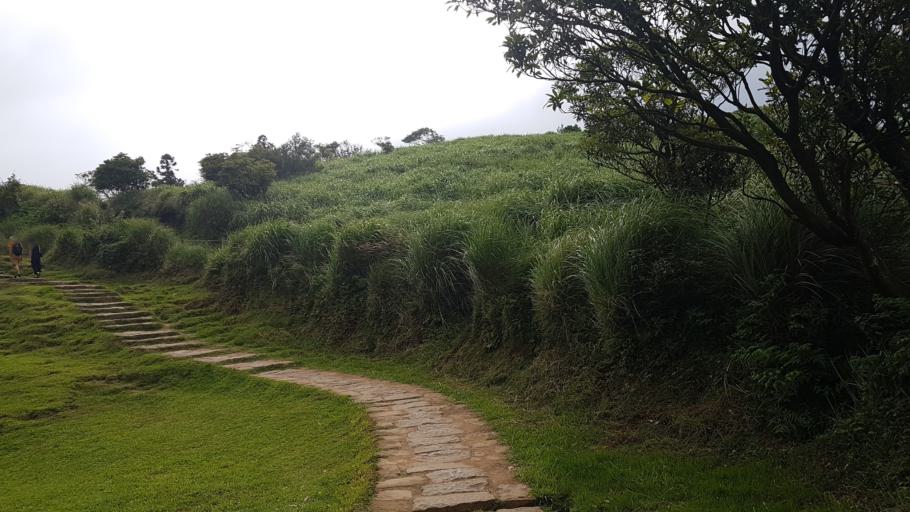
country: TW
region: Taipei
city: Taipei
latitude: 25.1671
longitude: 121.5758
